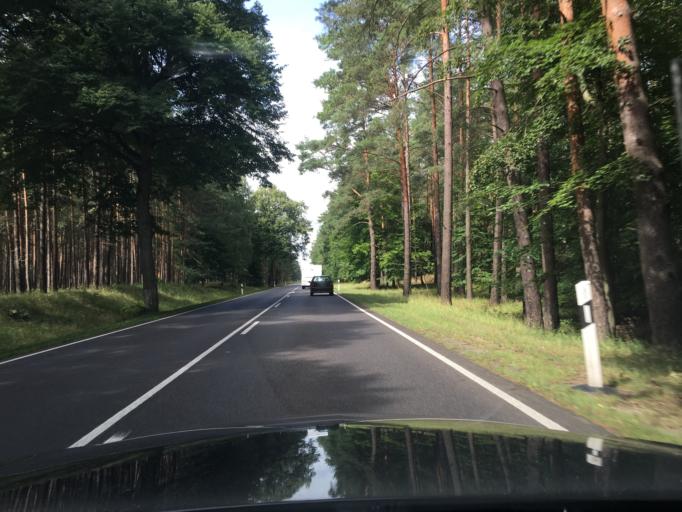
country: DE
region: Brandenburg
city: Furstenberg
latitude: 53.2668
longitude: 13.1155
